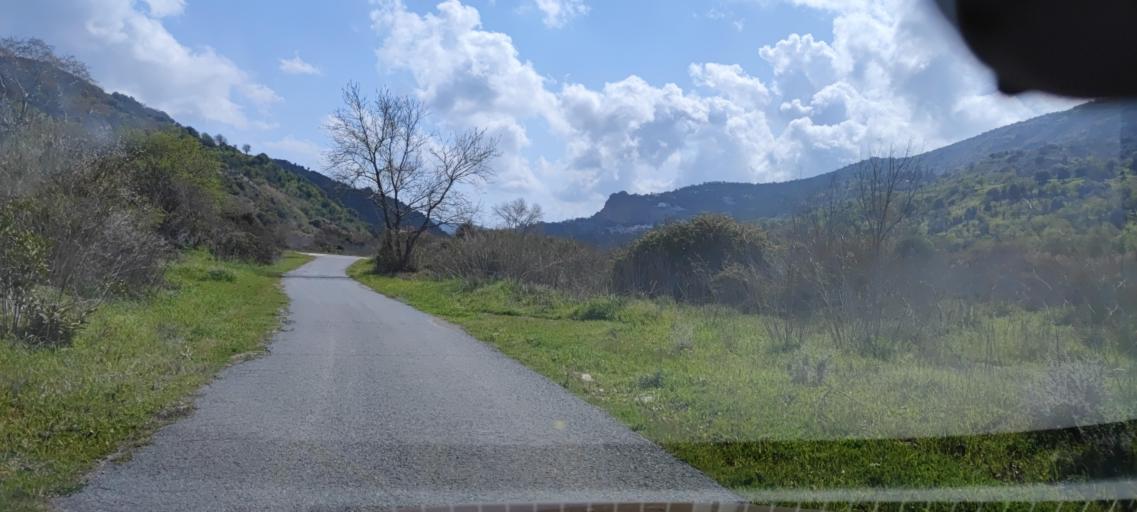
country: CY
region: Pafos
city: Mesogi
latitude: 34.8062
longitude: 32.5314
